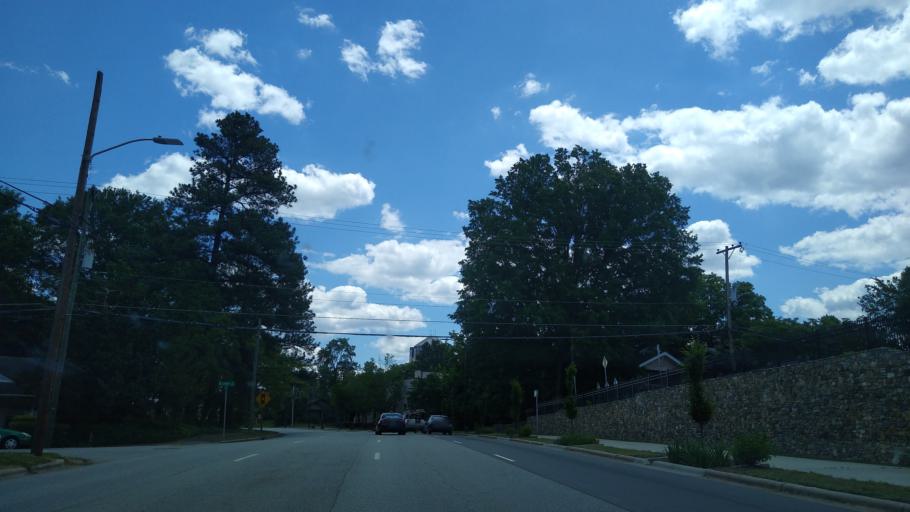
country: US
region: North Carolina
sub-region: Guilford County
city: Greensboro
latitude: 36.0785
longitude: -79.7985
